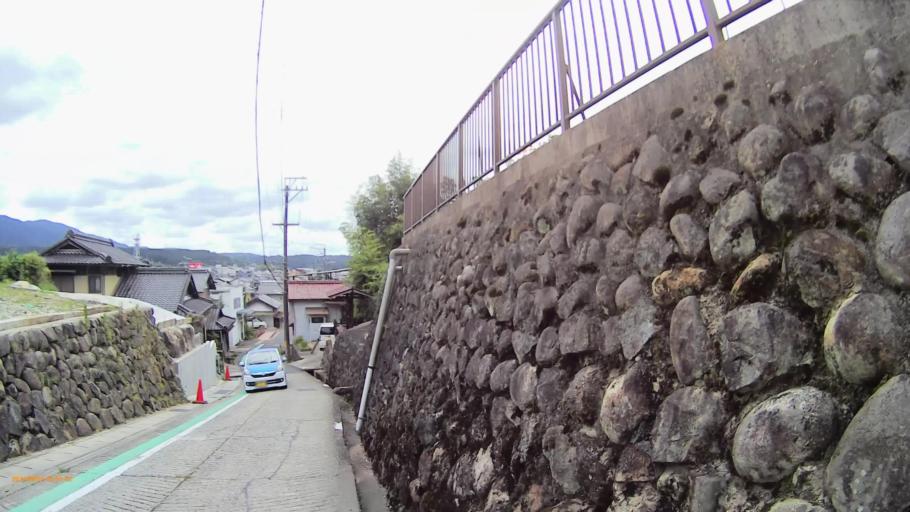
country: JP
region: Gifu
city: Nakatsugawa
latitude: 35.4567
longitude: 137.4152
